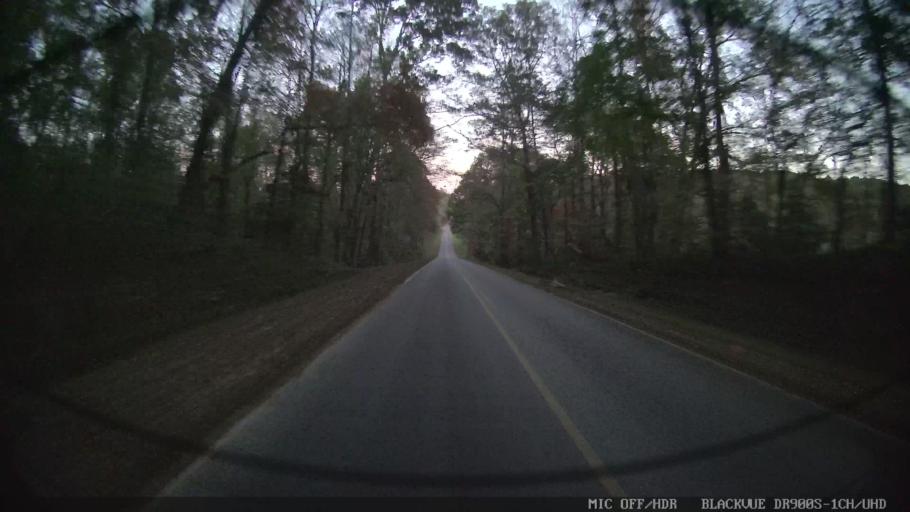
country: US
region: Georgia
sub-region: Union County
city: Blairsville
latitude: 34.9633
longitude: -83.8907
